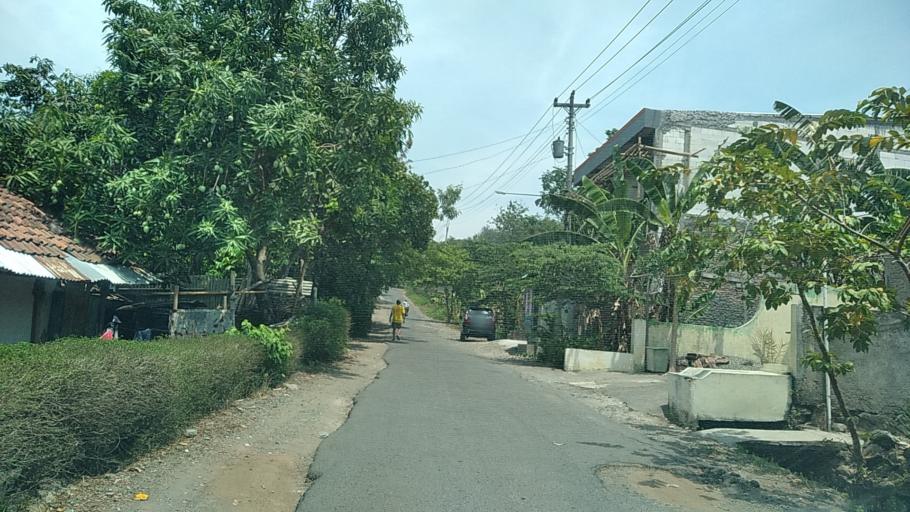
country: ID
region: Central Java
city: Mranggen
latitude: -7.0531
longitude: 110.4786
